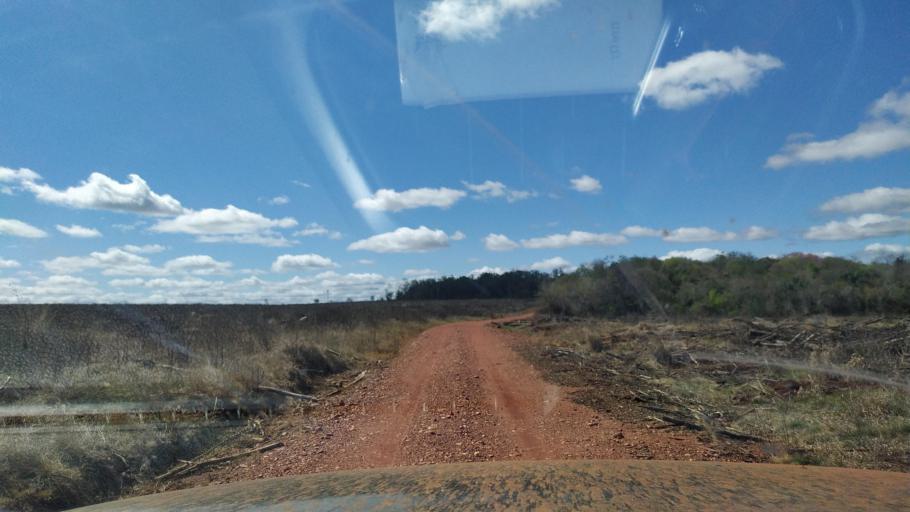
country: AR
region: Corrientes
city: Gobernador Ingeniero Valentin Virasoro
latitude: -28.2915
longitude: -56.0518
